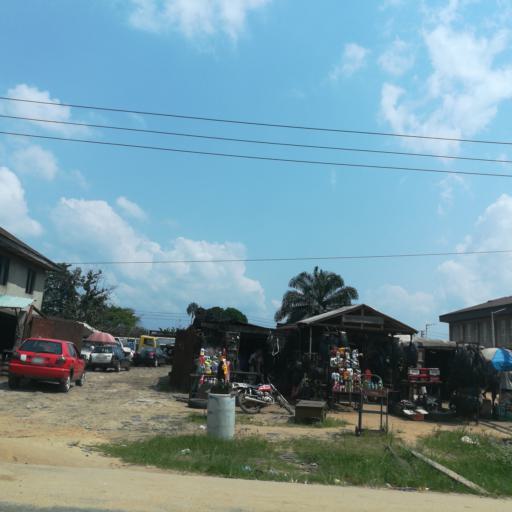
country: NG
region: Rivers
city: Port Harcourt
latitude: 4.8519
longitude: 7.0707
